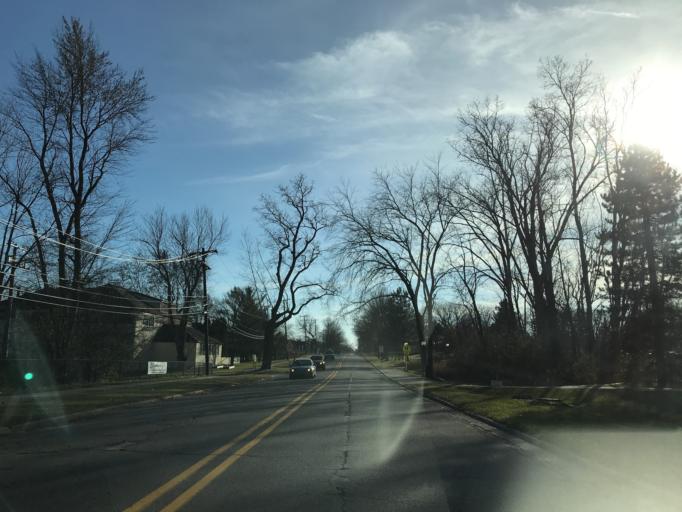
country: US
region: Michigan
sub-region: Washtenaw County
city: Ann Arbor
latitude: 42.2566
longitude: -83.7005
